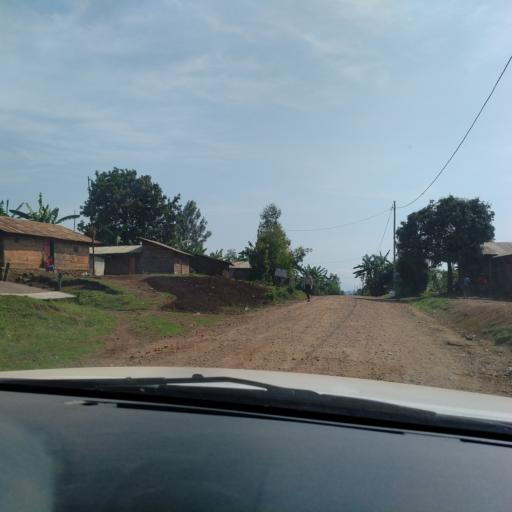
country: CD
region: South Kivu
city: Bukavu
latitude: -2.2194
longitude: 28.8298
